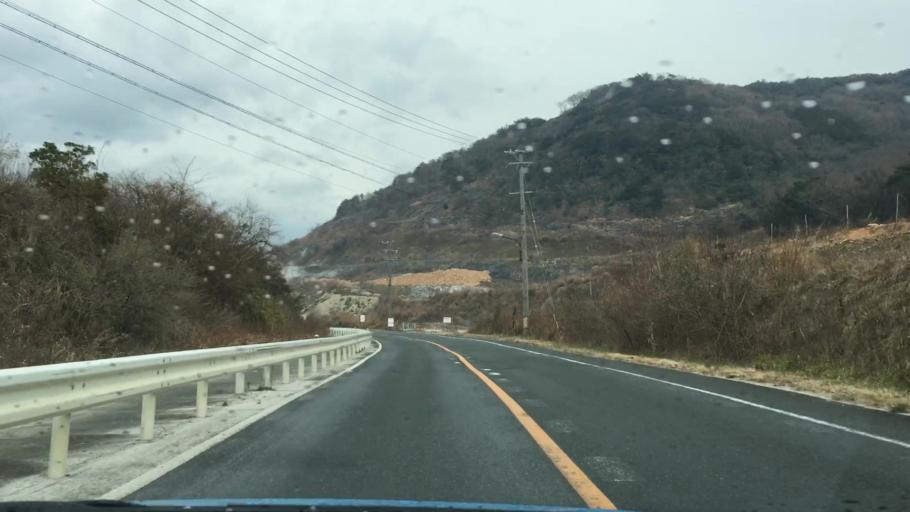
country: JP
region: Aichi
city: Tahara
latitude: 34.6803
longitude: 137.2512
